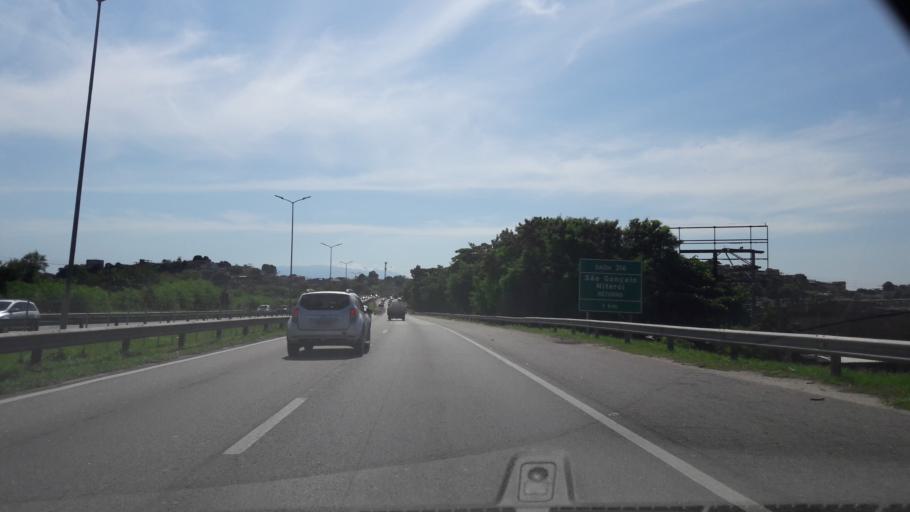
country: BR
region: Rio de Janeiro
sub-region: Sao Goncalo
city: Sao Goncalo
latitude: -22.8375
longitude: -43.0950
